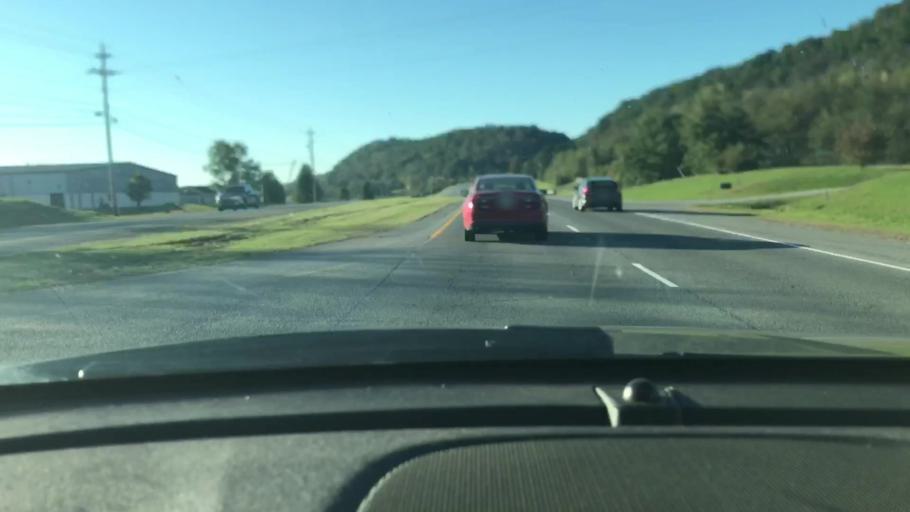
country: US
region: Tennessee
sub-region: Cheatham County
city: Ashland City
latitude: 36.2273
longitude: -87.0112
